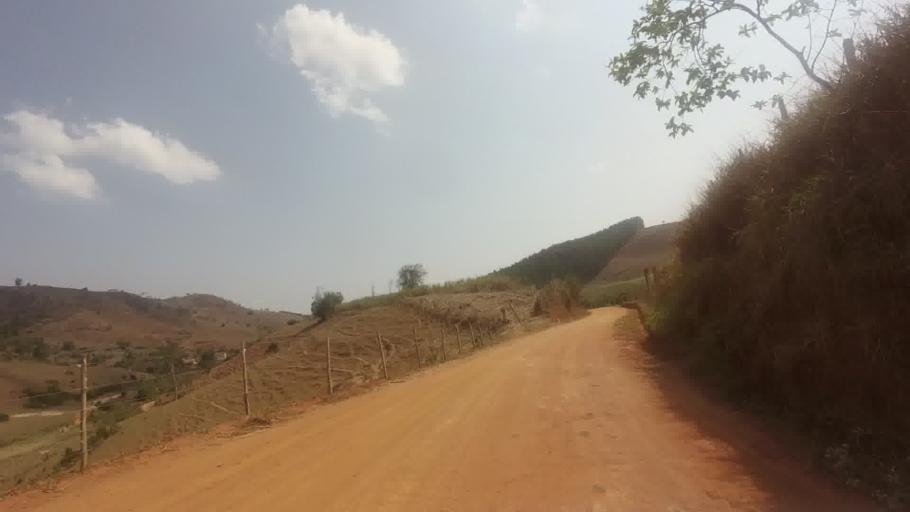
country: BR
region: Espirito Santo
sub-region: Sao Jose Do Calcado
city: Sao Jose do Calcado
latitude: -21.0490
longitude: -41.5240
